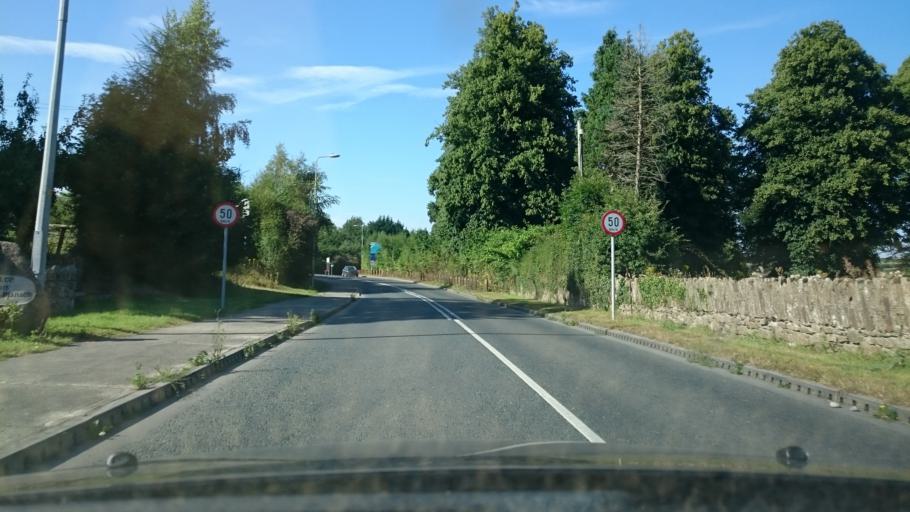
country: IE
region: Leinster
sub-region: Kilkenny
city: Graiguenamanagh
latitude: 52.5364
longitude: -6.9627
